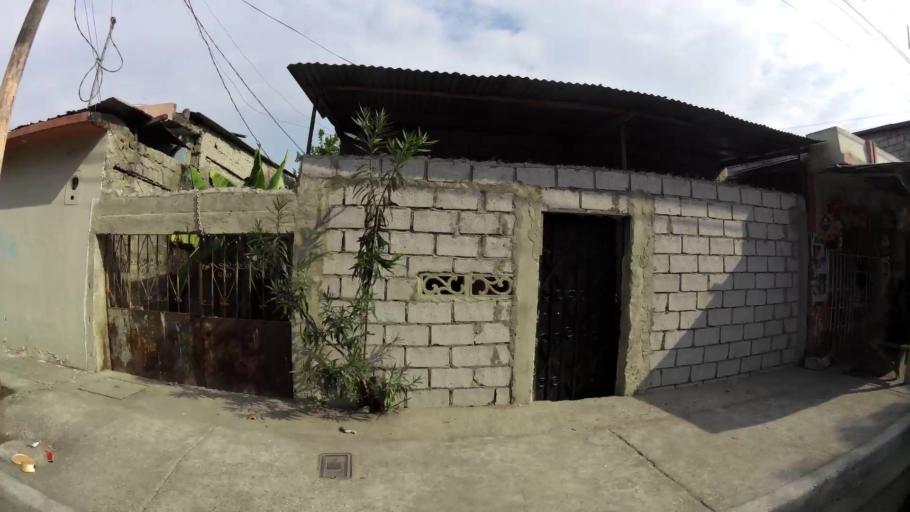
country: EC
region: Guayas
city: Guayaquil
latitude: -2.2503
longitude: -79.9088
